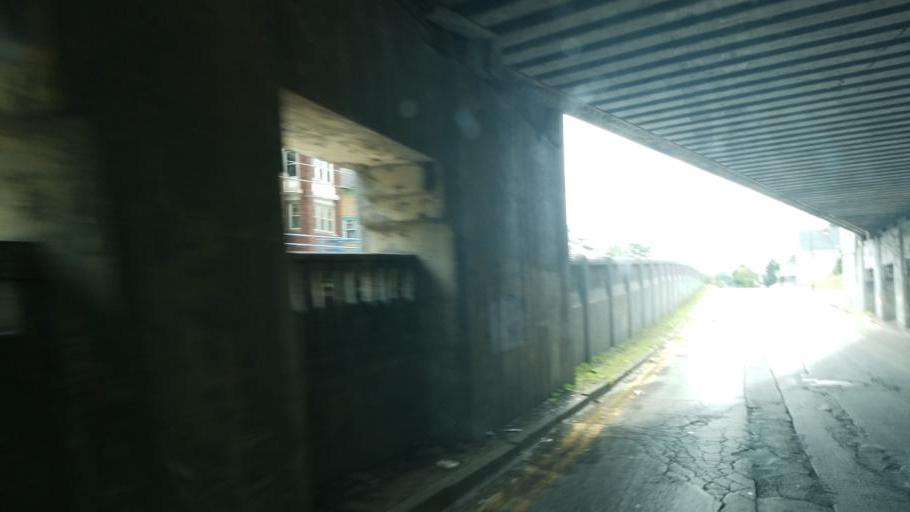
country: US
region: Ohio
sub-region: Wood County
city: Rossford
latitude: 41.6238
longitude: -83.5696
